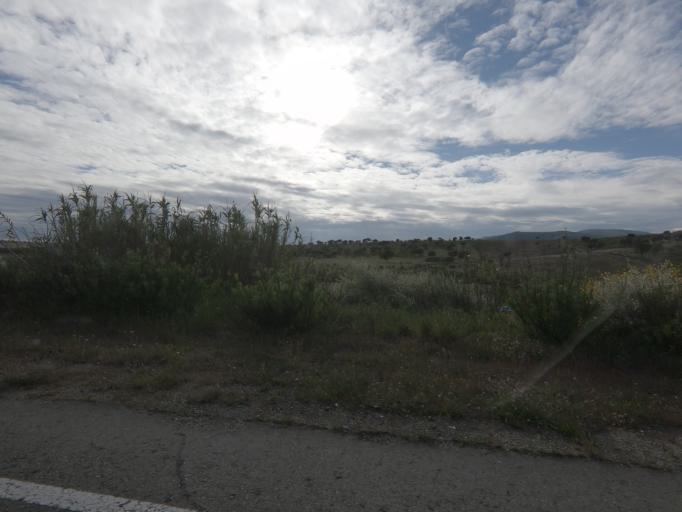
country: ES
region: Extremadura
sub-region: Provincia de Caceres
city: Perales del Puerto
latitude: 40.1138
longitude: -6.6705
